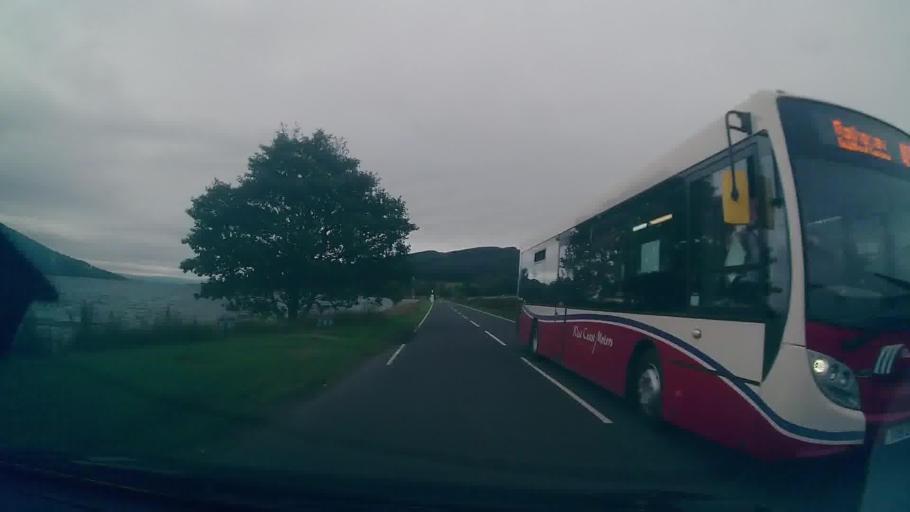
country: GB
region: Scotland
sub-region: Argyll and Bute
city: Port Bannatyne
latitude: 55.9202
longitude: -5.1585
